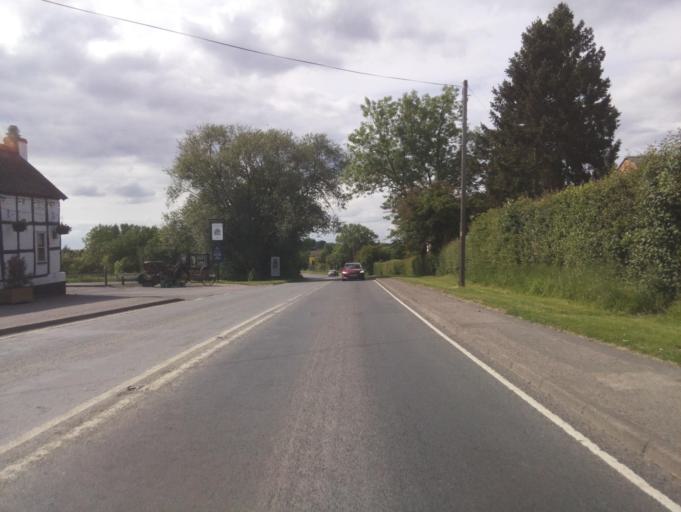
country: GB
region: England
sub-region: Worcestershire
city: Pershore
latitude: 52.1361
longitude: -2.1161
